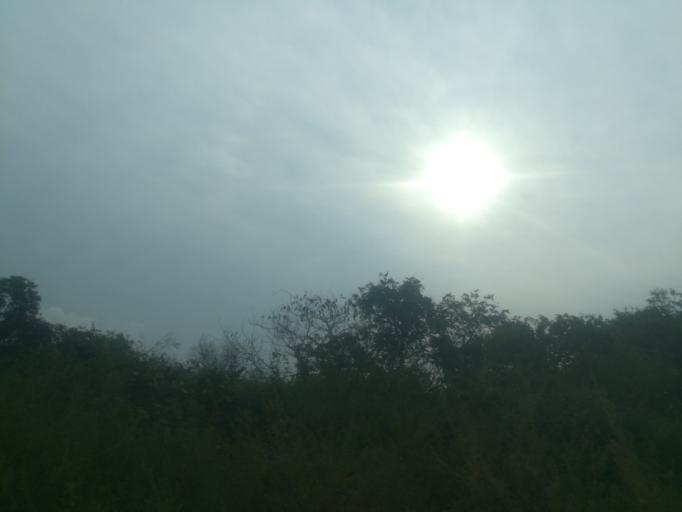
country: NG
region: Ogun
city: Ayetoro
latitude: 7.2563
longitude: 3.1139
